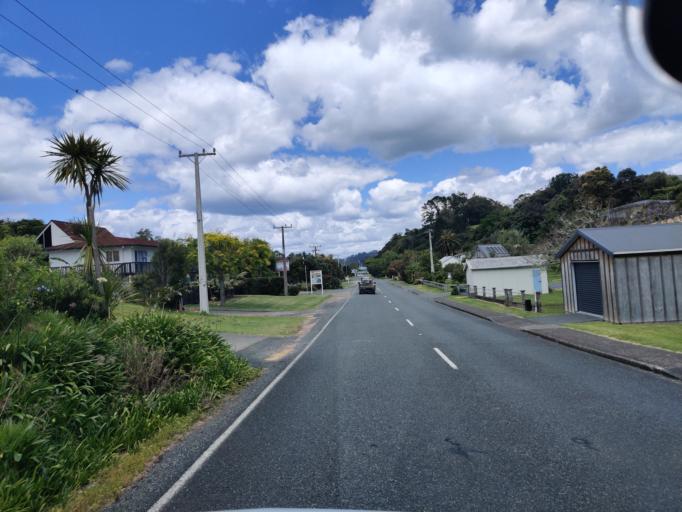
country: NZ
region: Northland
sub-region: Far North District
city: Paihia
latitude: -35.2649
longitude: 174.1243
